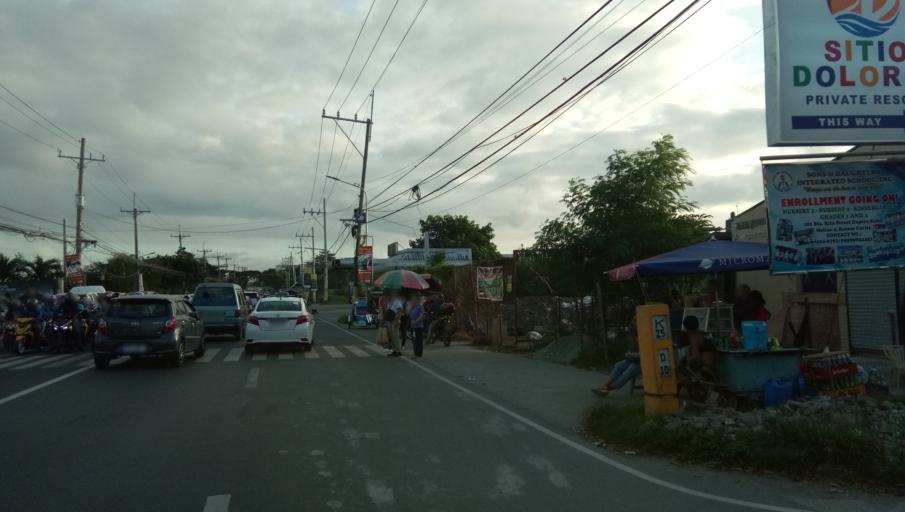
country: PH
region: Calabarzon
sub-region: Province of Cavite
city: Imus
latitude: 14.3801
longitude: 120.9788
